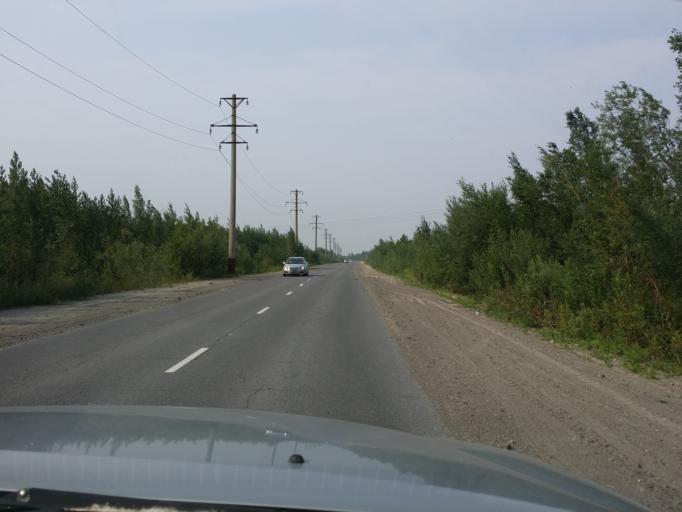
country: RU
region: Khanty-Mansiyskiy Avtonomnyy Okrug
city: Nizhnevartovsk
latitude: 61.0104
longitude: 76.5481
